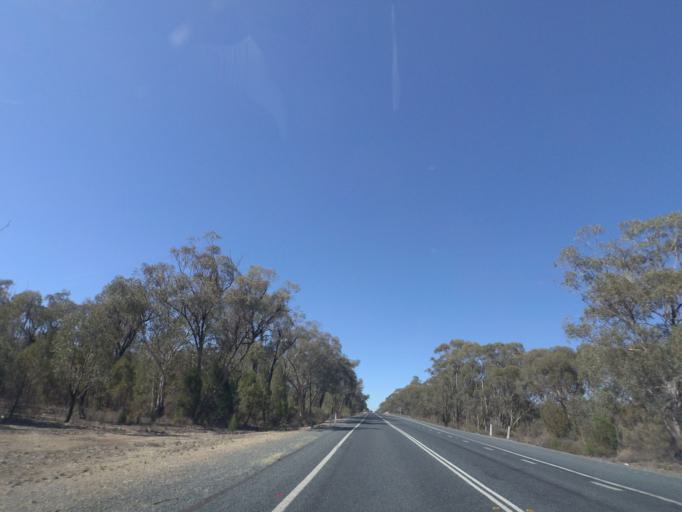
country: AU
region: New South Wales
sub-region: Bland
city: West Wyalong
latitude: -34.1249
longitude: 147.1259
